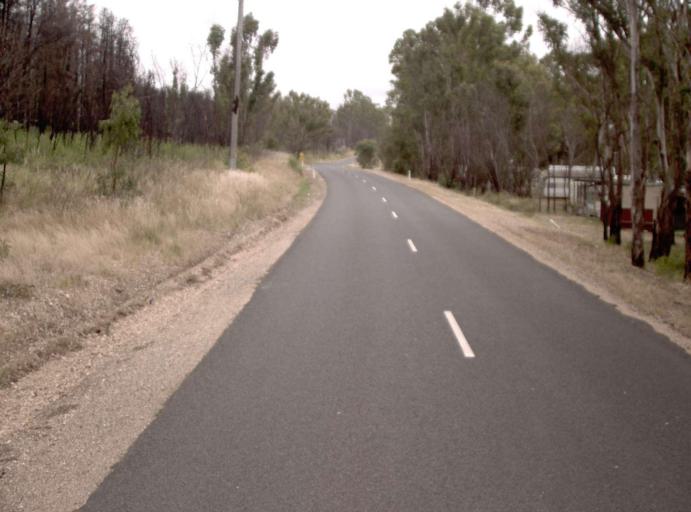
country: AU
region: Victoria
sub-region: Wellington
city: Heyfield
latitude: -37.9088
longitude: 146.7555
